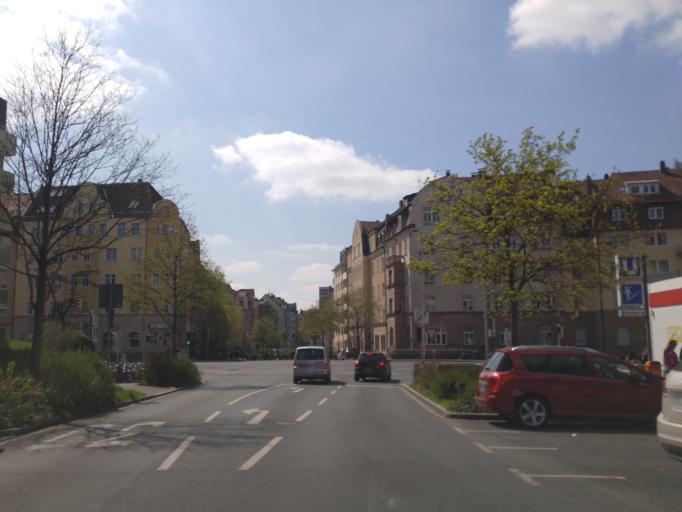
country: DE
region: Bavaria
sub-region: Regierungsbezirk Mittelfranken
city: Nuernberg
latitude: 49.4658
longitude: 11.1010
